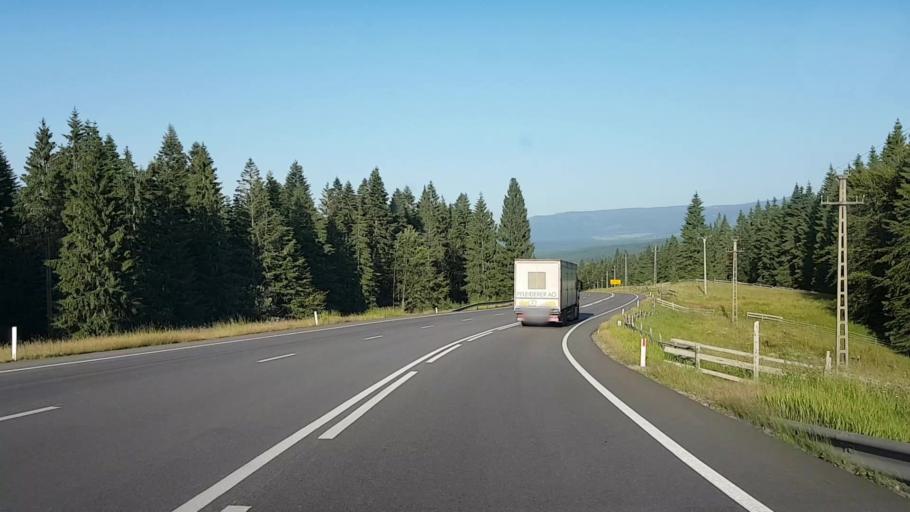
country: RO
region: Suceava
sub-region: Comuna Poiana Stampei
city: Poiana Stampei
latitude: 47.2848
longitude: 25.0420
